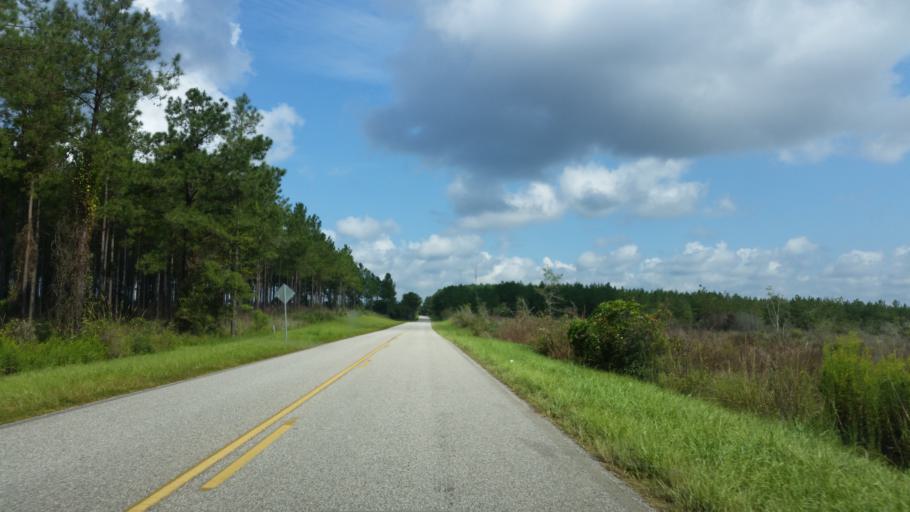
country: US
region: Florida
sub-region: Escambia County
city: Cantonment
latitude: 30.6746
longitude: -87.4704
